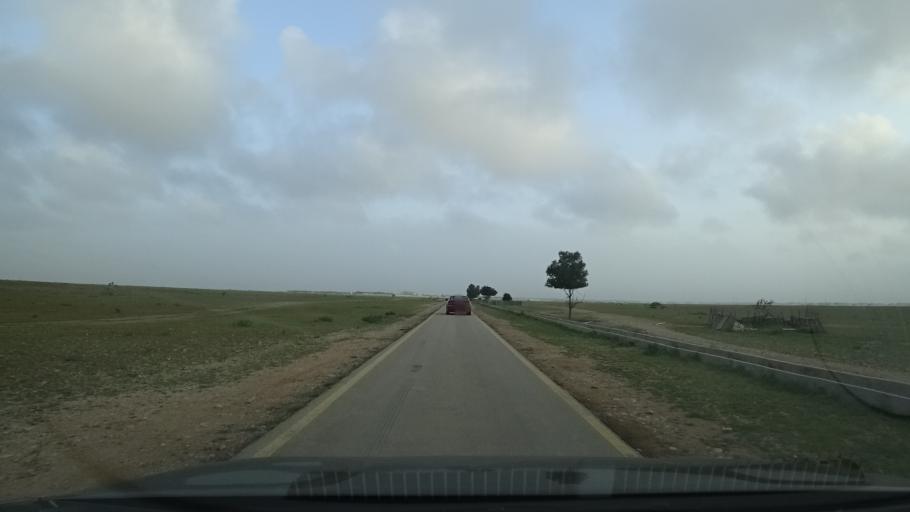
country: OM
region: Zufar
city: Salalah
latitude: 17.0851
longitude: 54.2321
